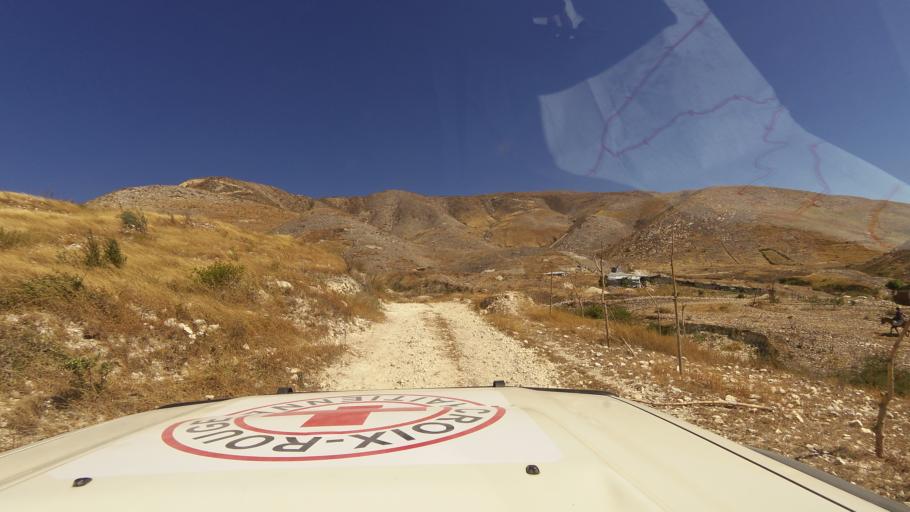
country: HT
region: Ouest
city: Croix des Bouquets
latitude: 18.6777
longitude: -72.2854
